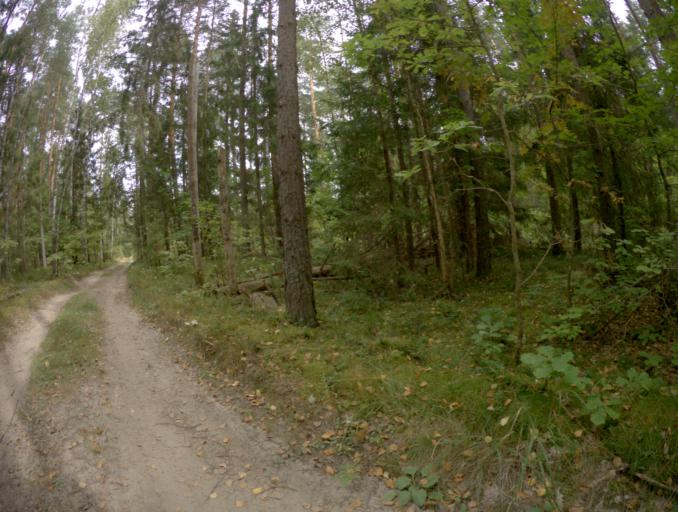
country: RU
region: Vladimir
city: Orgtrud
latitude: 56.1164
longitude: 40.7139
